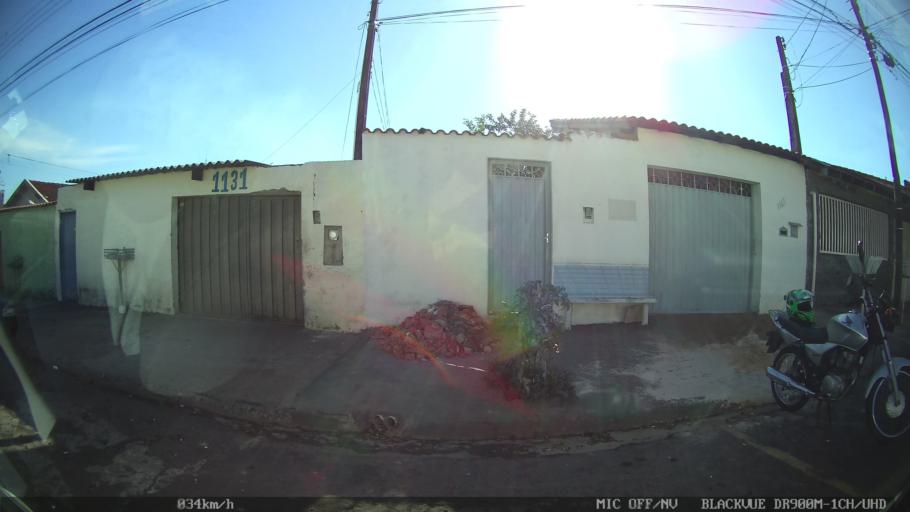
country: BR
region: Sao Paulo
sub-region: Franca
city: Franca
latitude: -20.5034
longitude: -47.4181
